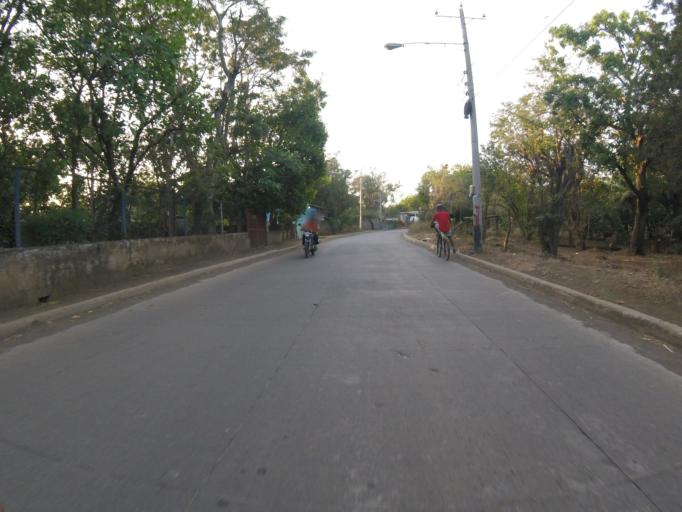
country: NI
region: Masaya
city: Ticuantepe
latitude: 12.0852
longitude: -86.1934
